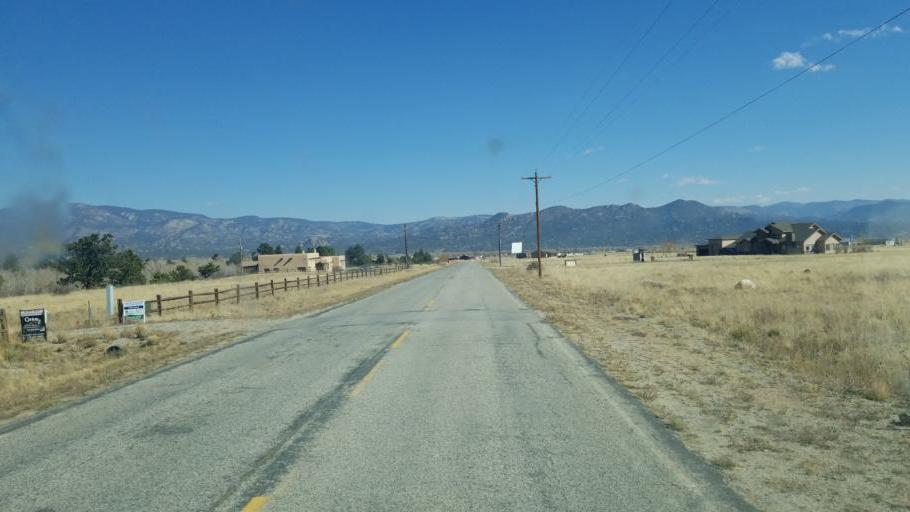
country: US
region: Colorado
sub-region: Chaffee County
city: Buena Vista
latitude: 38.8193
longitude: -106.1916
